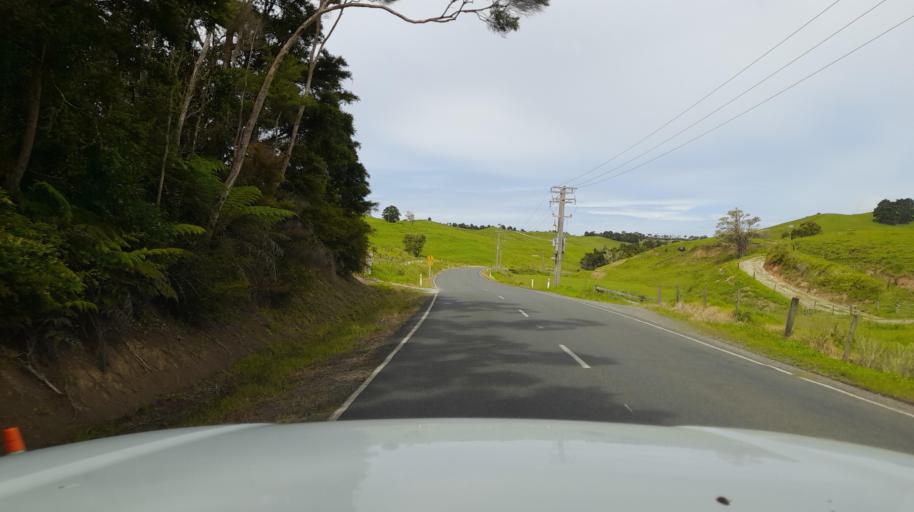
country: NZ
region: Northland
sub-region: Far North District
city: Taipa
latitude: -35.2693
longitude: 173.4914
